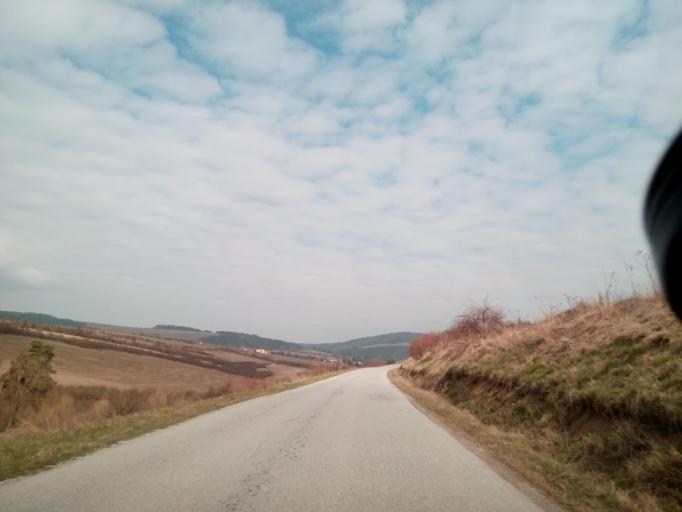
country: SK
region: Presovsky
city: Sabinov
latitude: 49.0312
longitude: 21.0189
